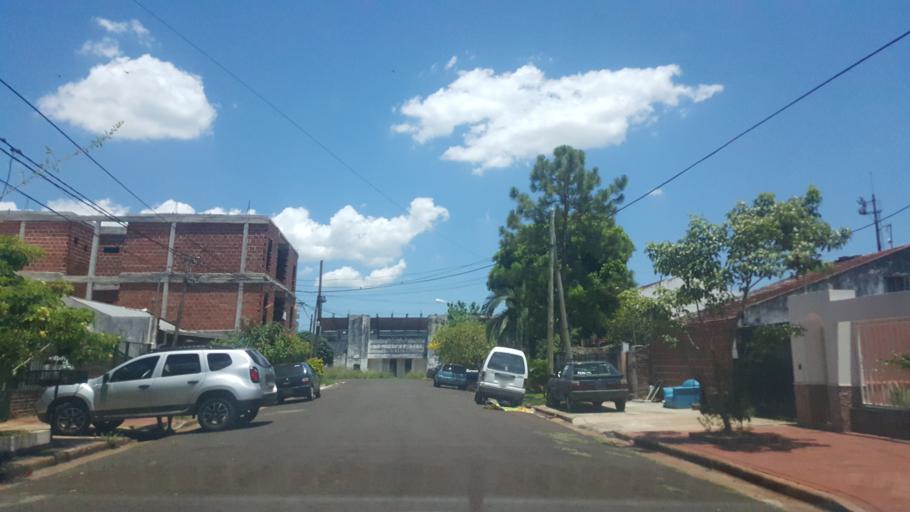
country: AR
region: Misiones
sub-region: Departamento de Capital
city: Posadas
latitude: -27.3681
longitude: -55.9060
